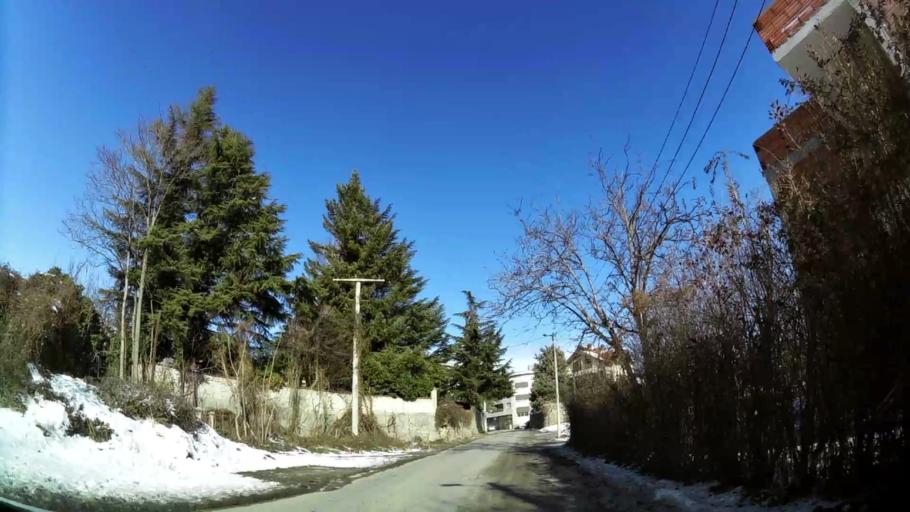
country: MK
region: Saraj
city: Saraj
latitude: 41.9966
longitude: 21.3262
